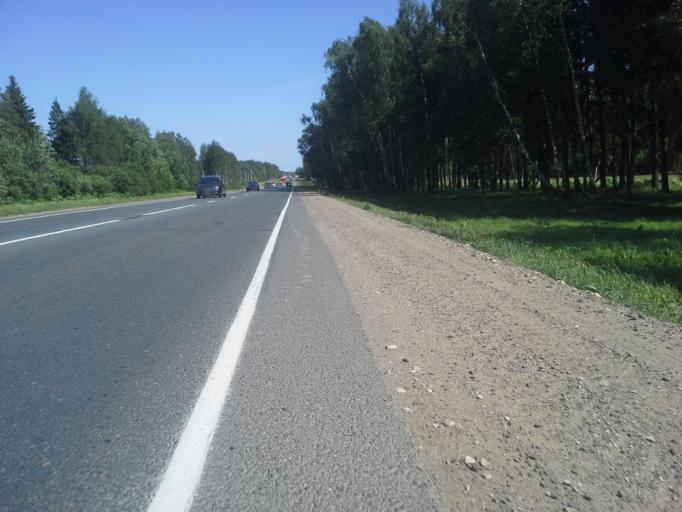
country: RU
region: Moskovskaya
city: Troitsk
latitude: 55.4032
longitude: 37.2176
